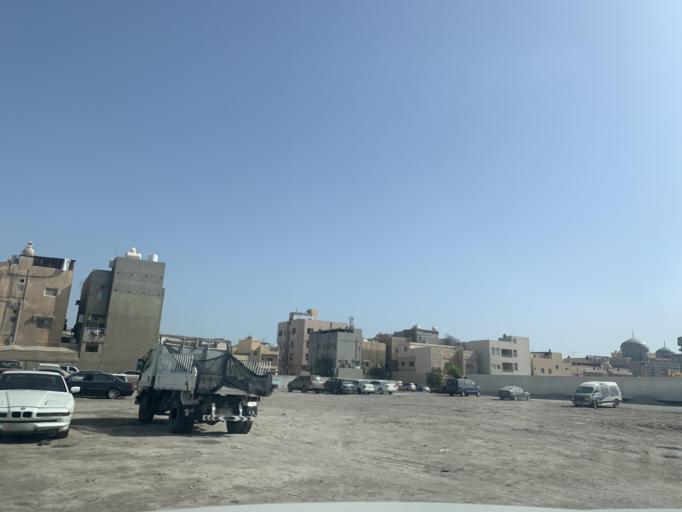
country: BH
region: Manama
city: Jidd Hafs
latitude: 26.2091
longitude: 50.5600
